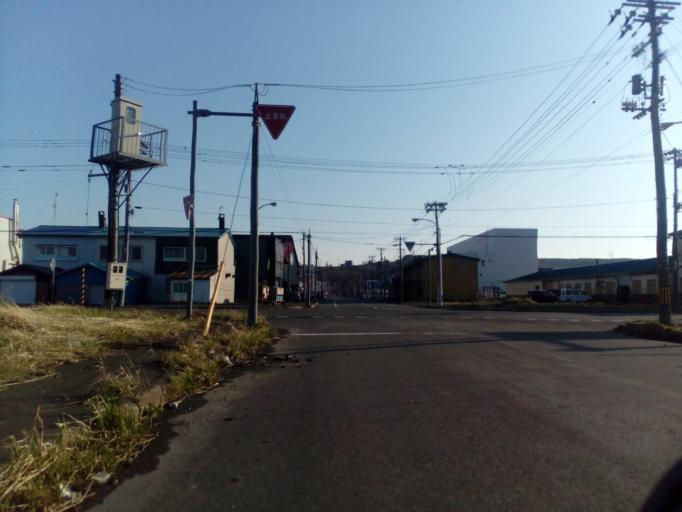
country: JP
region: Hokkaido
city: Wakkanai
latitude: 45.4026
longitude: 141.6876
